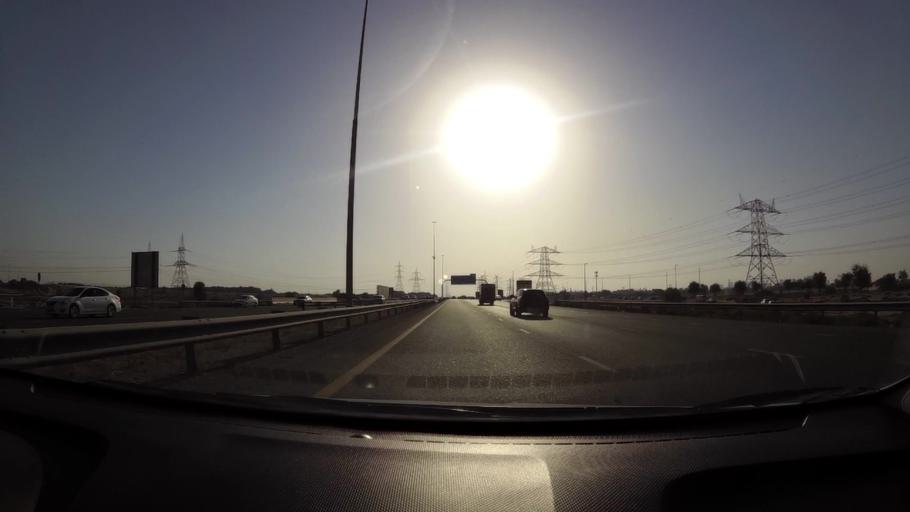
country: AE
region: Ajman
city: Ajman
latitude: 25.3576
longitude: 55.4981
